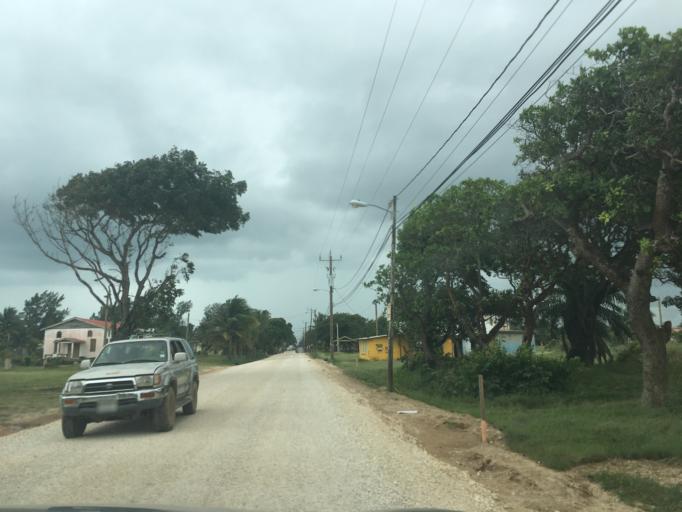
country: BZ
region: Stann Creek
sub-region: Dangriga
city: Dangriga
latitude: 16.8601
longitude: -88.2832
